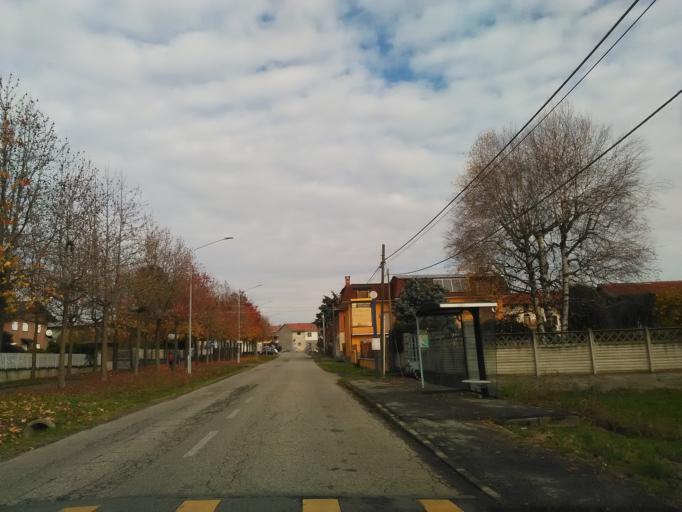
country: IT
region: Piedmont
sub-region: Provincia di Vercelli
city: Alice Castello
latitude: 45.3636
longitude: 8.0703
